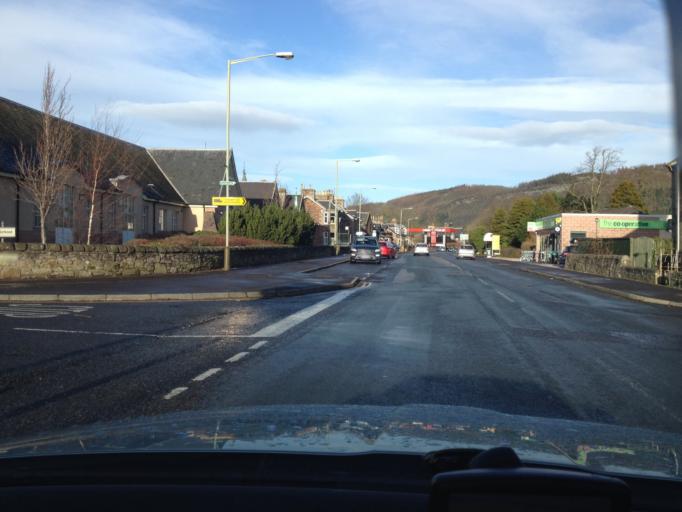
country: GB
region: Scotland
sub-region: Perth and Kinross
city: Bridge of Earn
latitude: 56.3493
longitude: -3.4067
